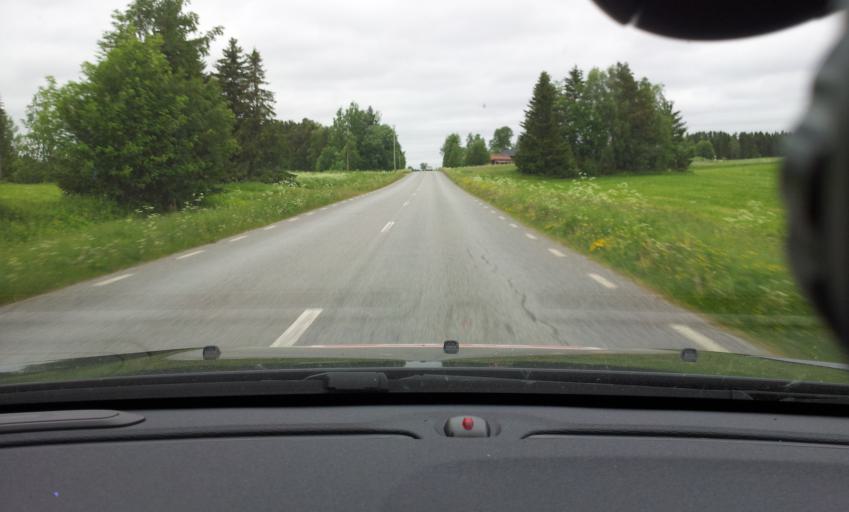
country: SE
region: Jaemtland
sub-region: Krokoms Kommun
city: Krokom
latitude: 63.1412
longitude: 14.1849
